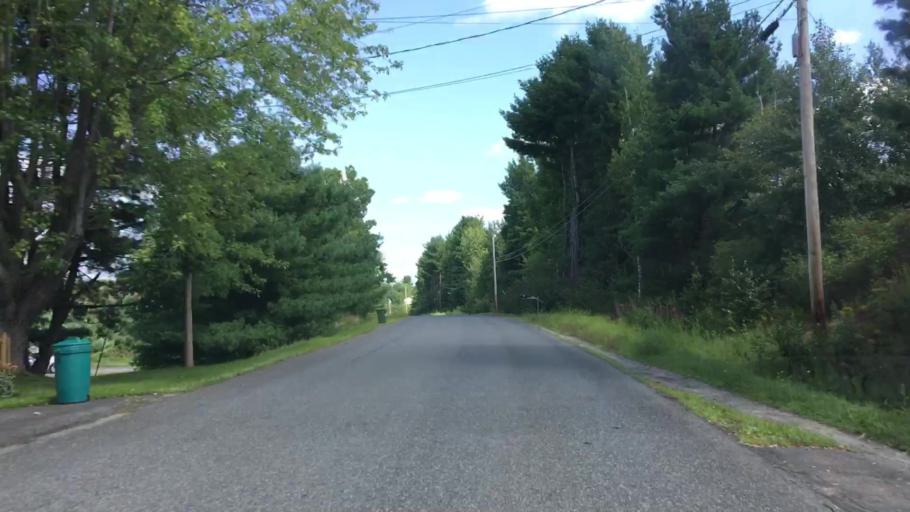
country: US
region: Maine
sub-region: Kennebec County
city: Manchester
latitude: 44.3571
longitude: -69.8163
